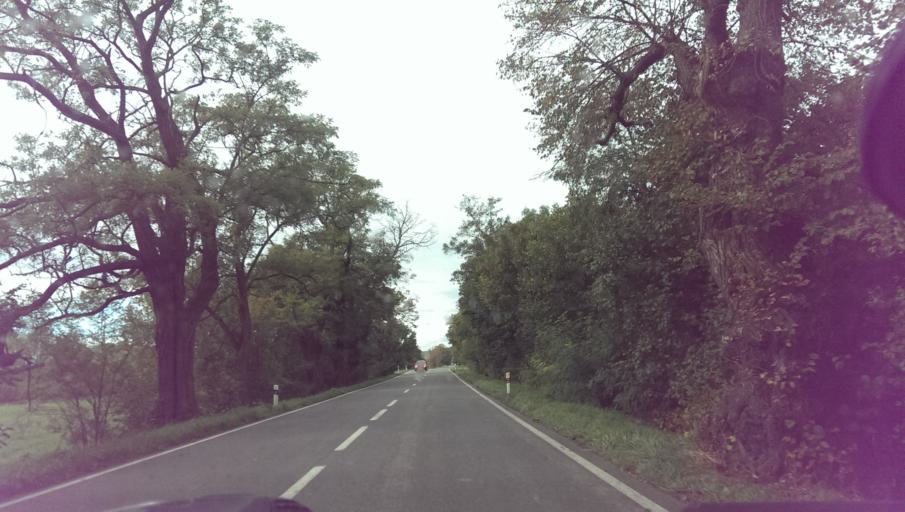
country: CZ
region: South Moravian
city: Moravsky Pisek
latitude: 48.9891
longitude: 17.3491
